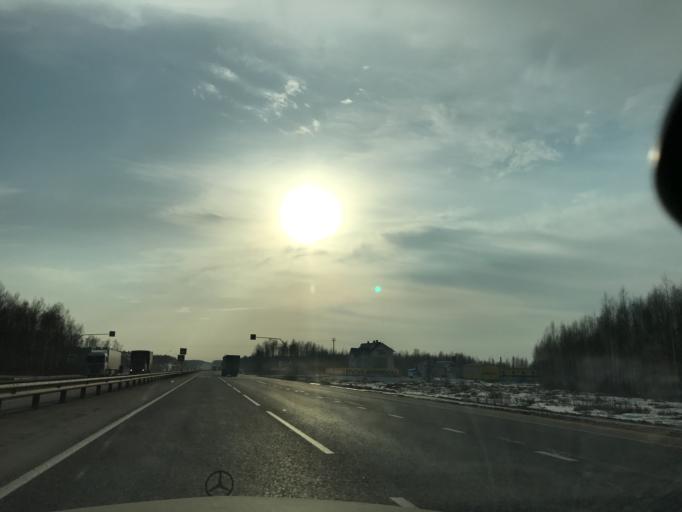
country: RU
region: Vladimir
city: Sudogda
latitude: 56.1361
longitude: 40.8891
